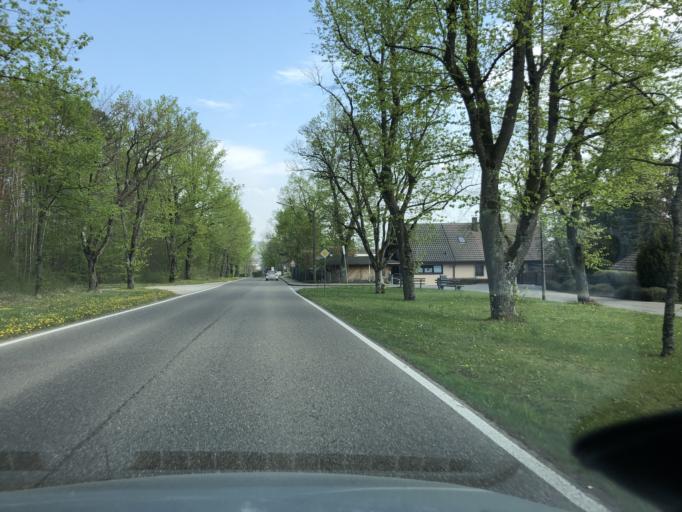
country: DE
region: Baden-Wuerttemberg
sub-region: Regierungsbezirk Stuttgart
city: Weil der Stadt
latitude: 48.7534
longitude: 8.8574
